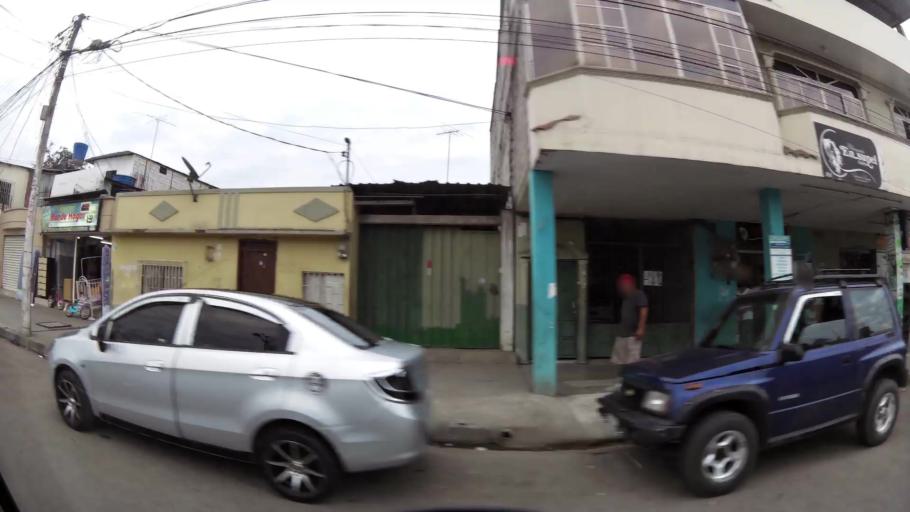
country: EC
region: El Oro
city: Machala
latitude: -3.2571
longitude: -79.9520
